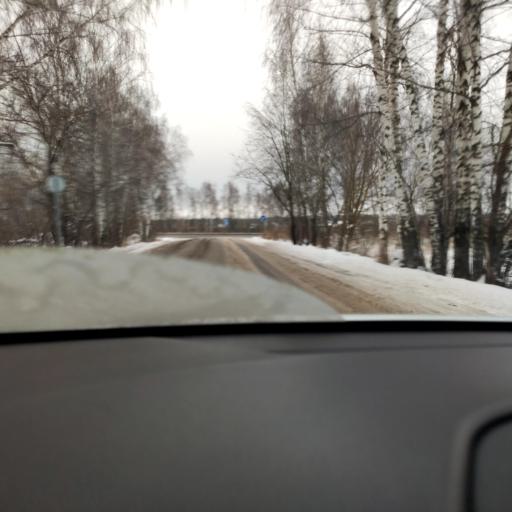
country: RU
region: Tatarstan
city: Osinovo
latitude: 55.8635
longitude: 48.8140
